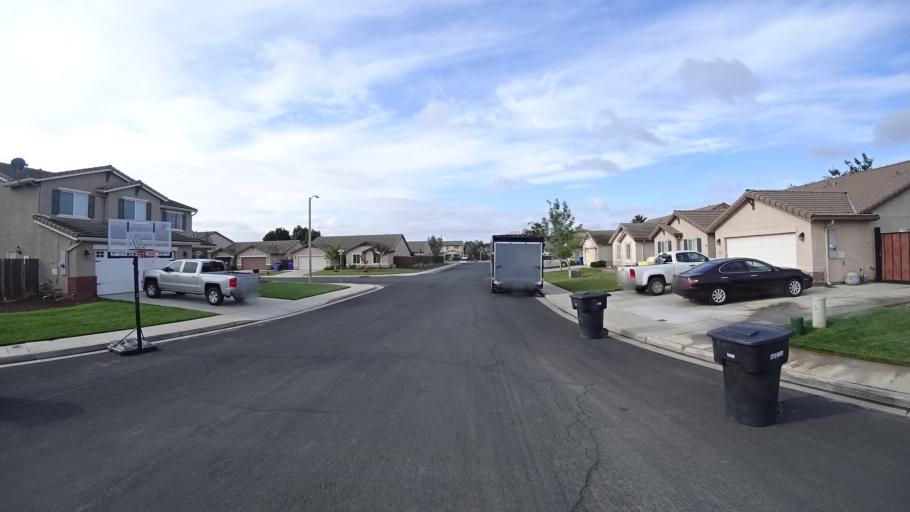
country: US
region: California
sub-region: Kings County
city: Lucerne
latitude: 36.3493
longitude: -119.6814
